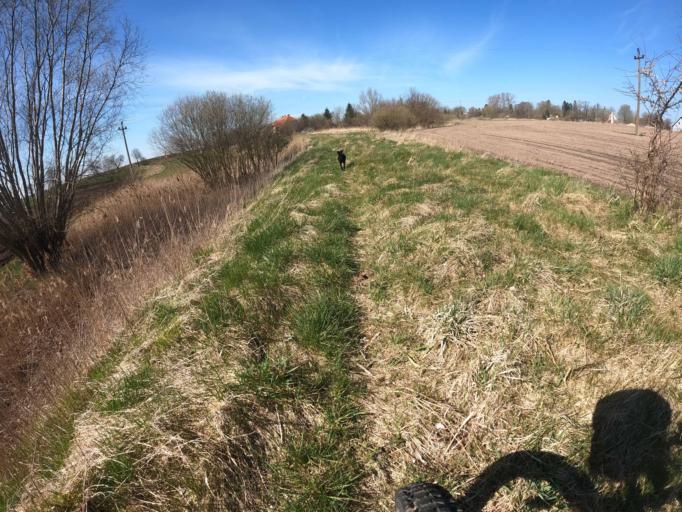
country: PL
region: West Pomeranian Voivodeship
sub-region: Powiat gryficki
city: Brojce
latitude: 53.9967
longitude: 15.3834
